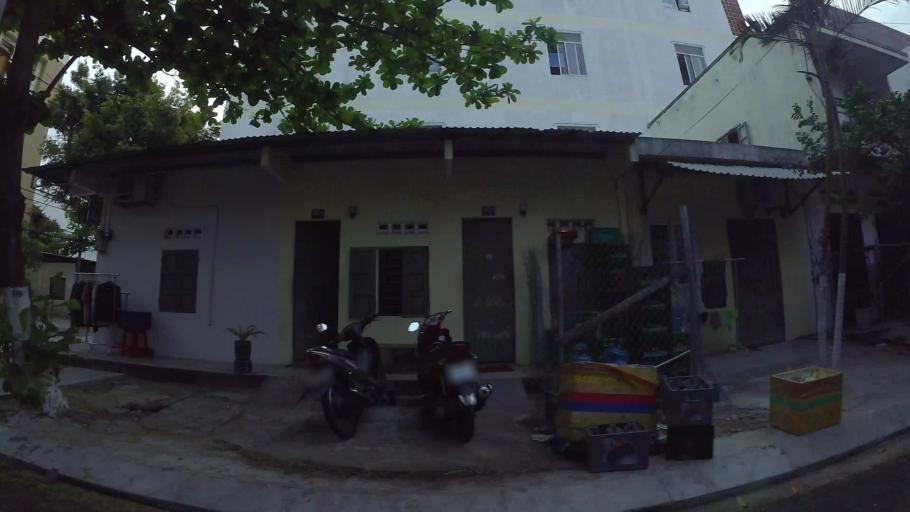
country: VN
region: Da Nang
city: Son Tra
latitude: 16.0478
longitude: 108.2453
